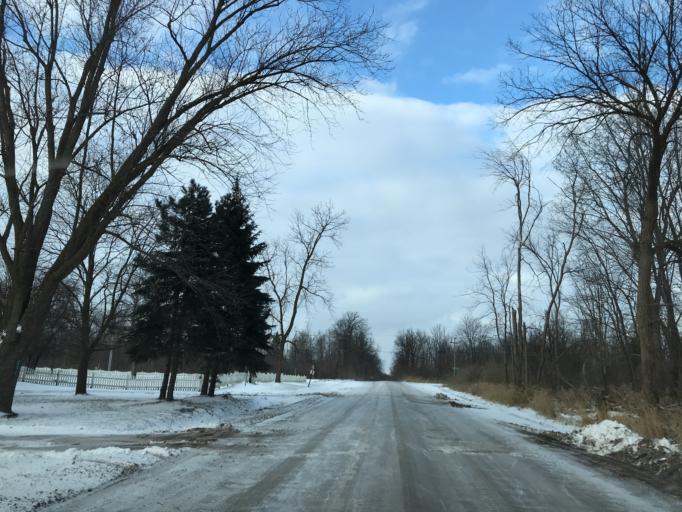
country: US
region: Michigan
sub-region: Oakland County
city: South Lyon
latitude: 42.4471
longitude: -83.5917
